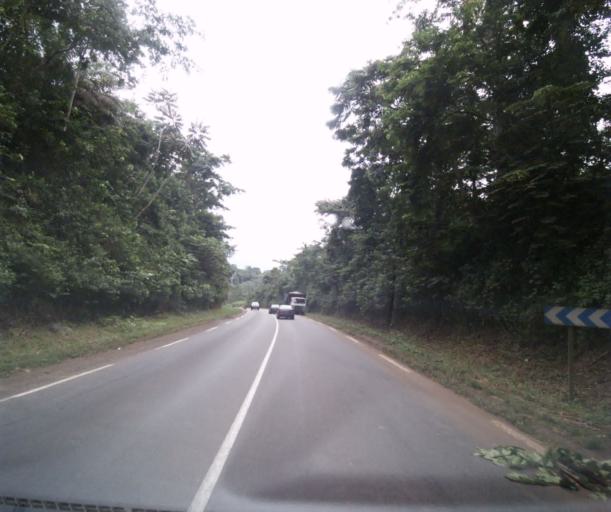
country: CM
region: Centre
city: Mbankomo
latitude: 3.7823
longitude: 11.2454
